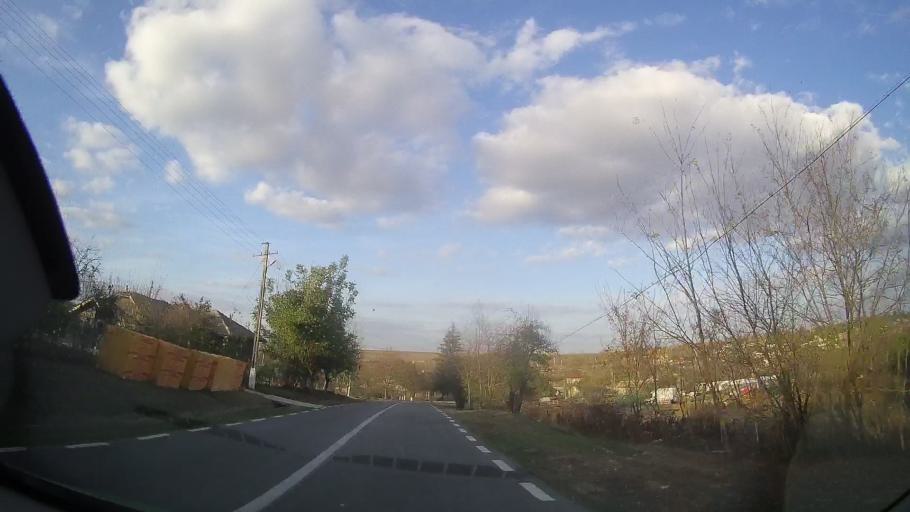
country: RO
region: Constanta
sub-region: Comuna Independenta
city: Independenta
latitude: 43.9529
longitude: 28.0752
